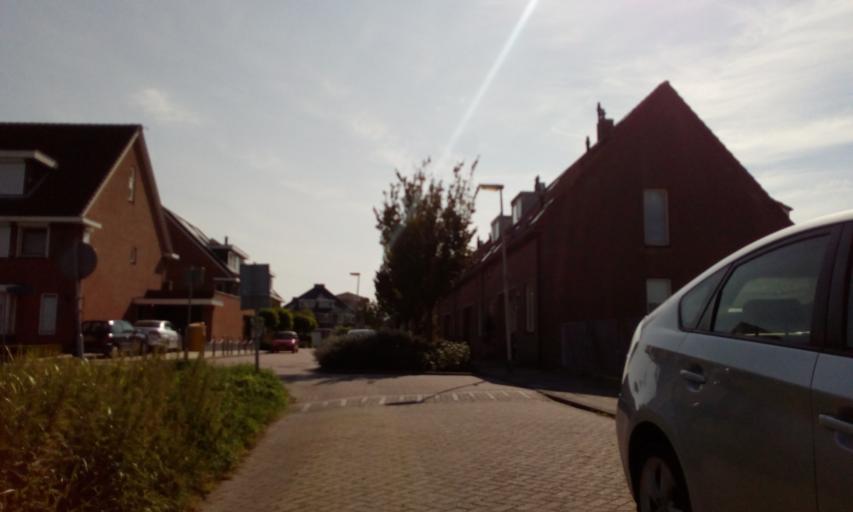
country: NL
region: South Holland
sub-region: Gemeente Waddinxveen
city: Groenswaard
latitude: 52.0458
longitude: 4.6393
